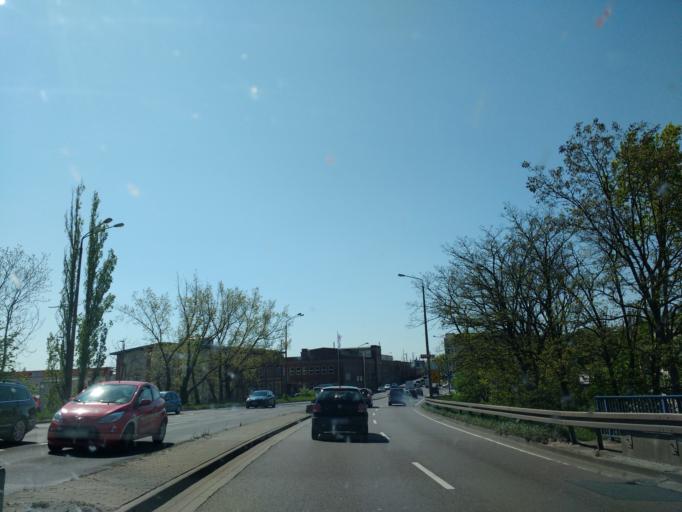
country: DE
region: Saxony-Anhalt
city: Halle (Saale)
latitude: 51.4890
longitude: 11.9843
